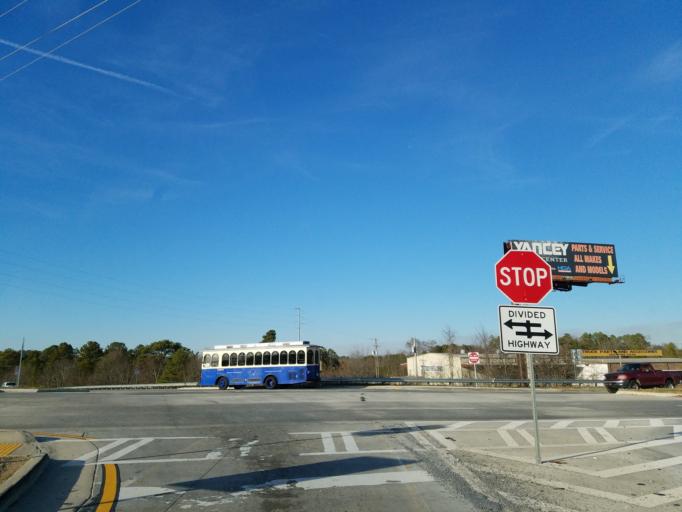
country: US
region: Georgia
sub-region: Gordon County
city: Calhoun
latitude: 34.5771
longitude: -84.9490
